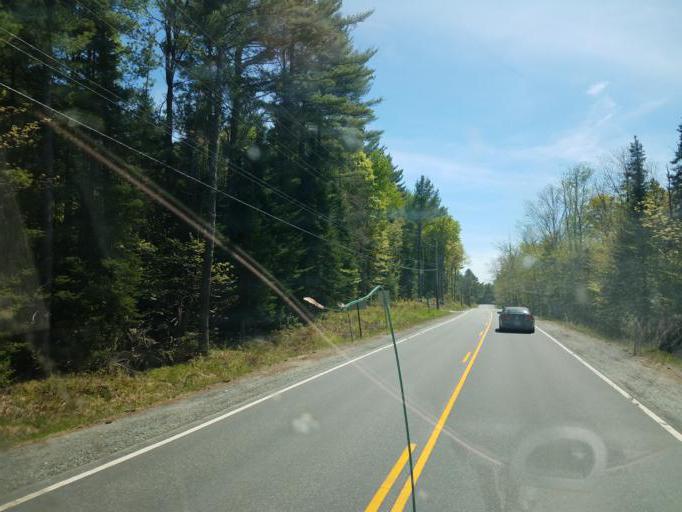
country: US
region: New Hampshire
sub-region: Grafton County
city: Grafton
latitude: 43.7127
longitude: -71.9608
